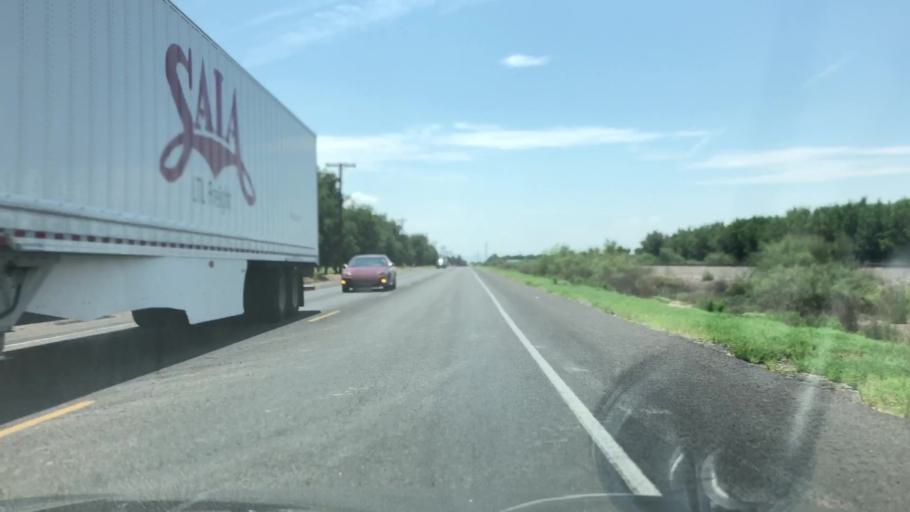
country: US
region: New Mexico
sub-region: Dona Ana County
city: Mesquite
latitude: 32.2140
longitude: -106.7278
